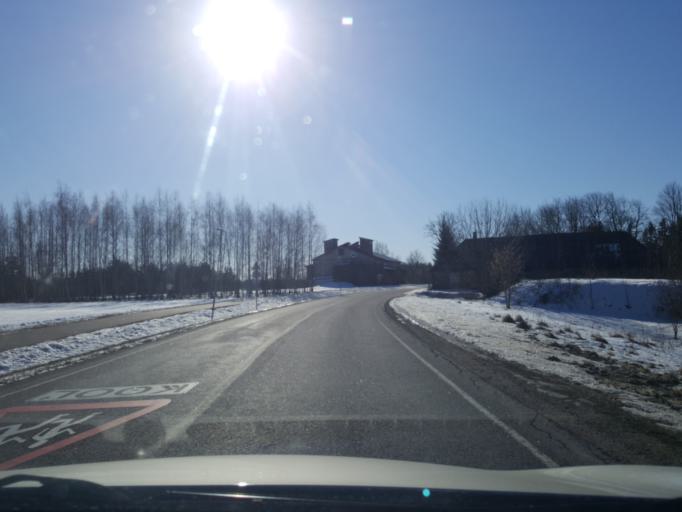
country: EE
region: Viljandimaa
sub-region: Viiratsi vald
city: Viiratsi
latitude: 58.4285
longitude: 25.6839
